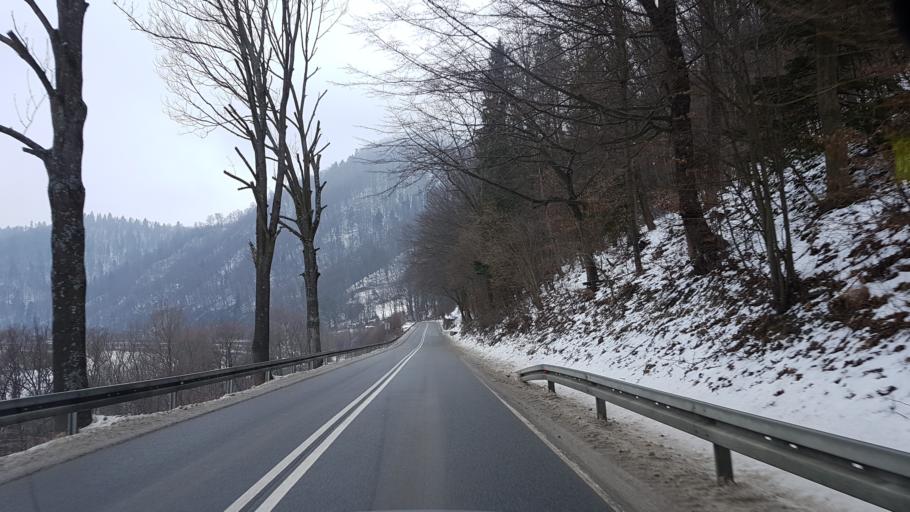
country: PL
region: Lesser Poland Voivodeship
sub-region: Powiat nowosadecki
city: Piwniczna-Zdroj
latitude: 49.4089
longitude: 20.7467
